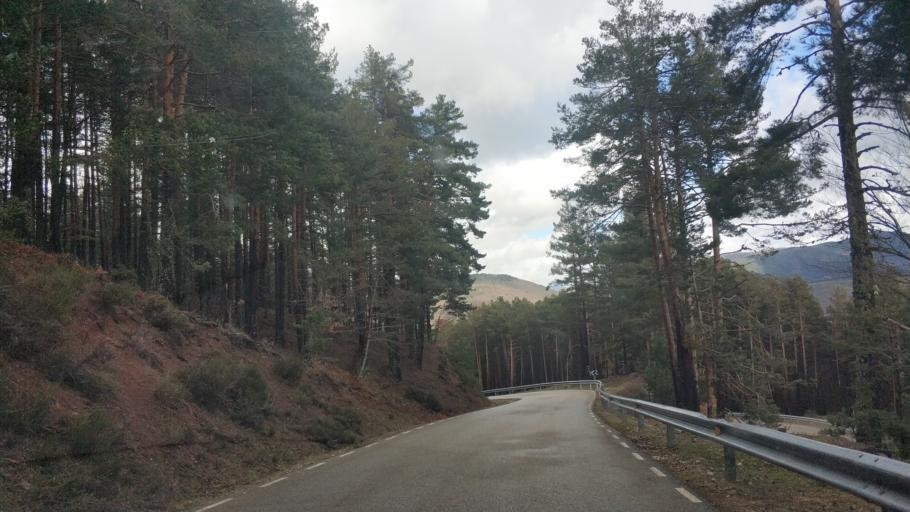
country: ES
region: Castille and Leon
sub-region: Provincia de Burgos
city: Neila
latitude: 42.0455
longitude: -3.0107
